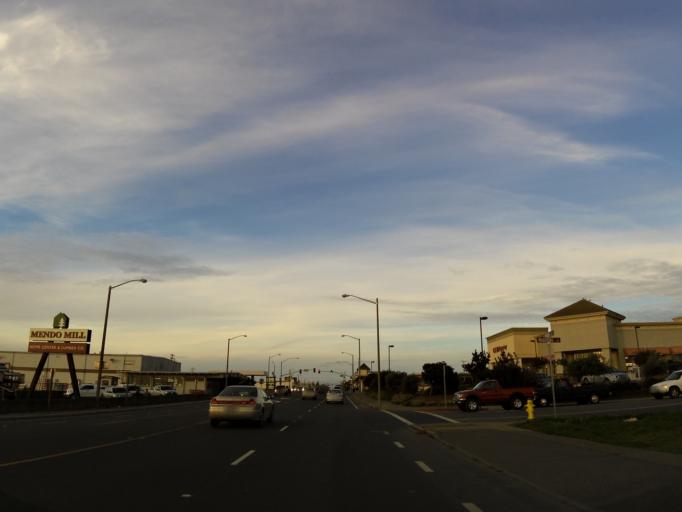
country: US
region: California
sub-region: Mendocino County
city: Fort Bragg
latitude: 39.4402
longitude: -123.8059
